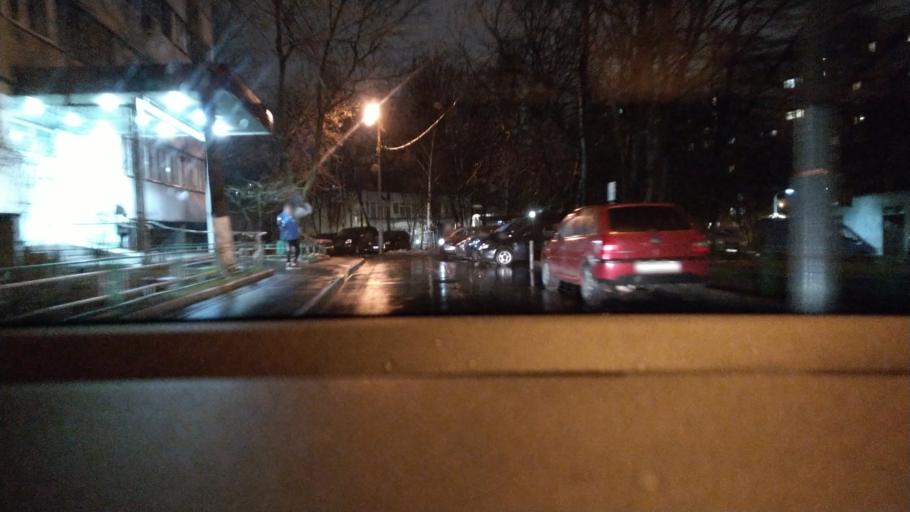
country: RU
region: Moscow
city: Orekhovo-Borisovo
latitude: 55.6190
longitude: 37.7055
